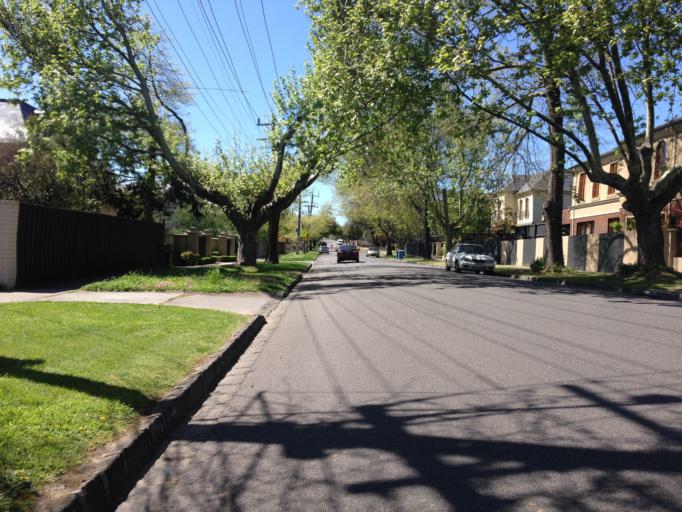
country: AU
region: Victoria
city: Balwyn
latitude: -37.8078
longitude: 145.0698
